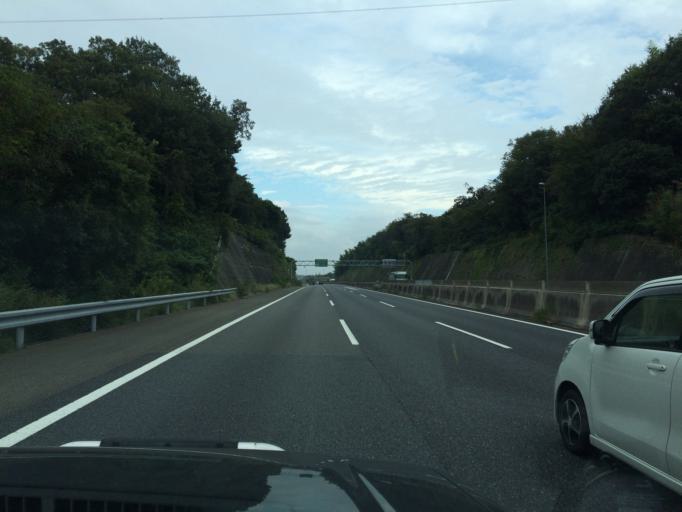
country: JP
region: Mie
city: Yokkaichi
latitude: 35.0206
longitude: 136.5955
